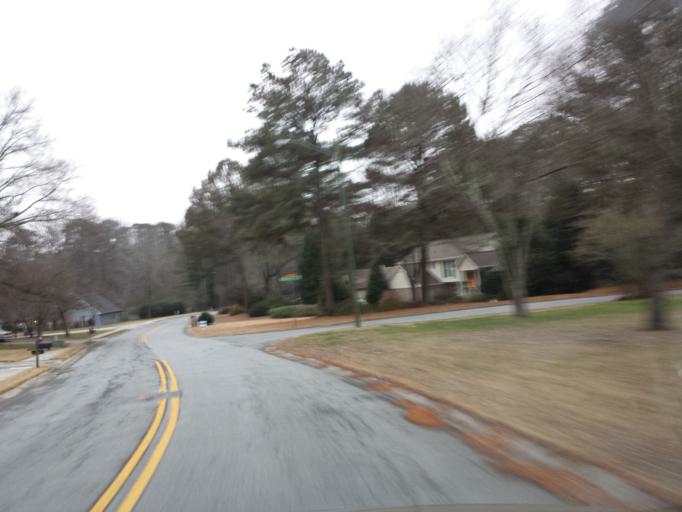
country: US
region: Georgia
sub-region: Fulton County
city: Sandy Springs
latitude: 33.9623
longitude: -84.4475
